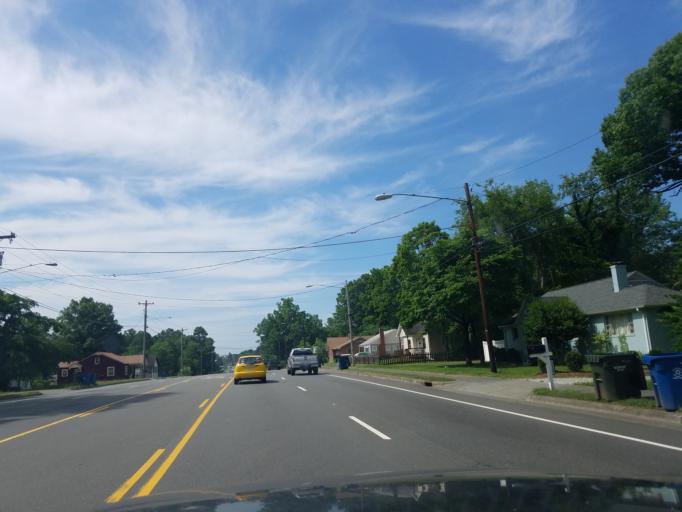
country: US
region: North Carolina
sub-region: Durham County
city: Durham
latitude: 36.0433
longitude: -78.9295
